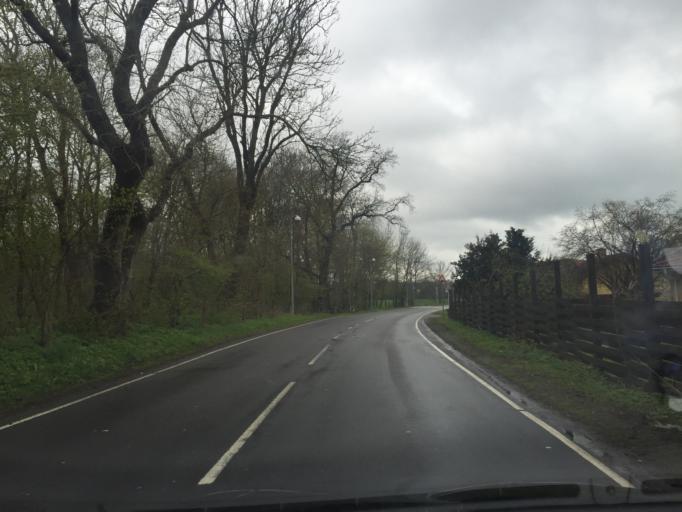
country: DK
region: Capital Region
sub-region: Hoje-Taastrup Kommune
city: Taastrup
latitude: 55.6829
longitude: 12.2503
